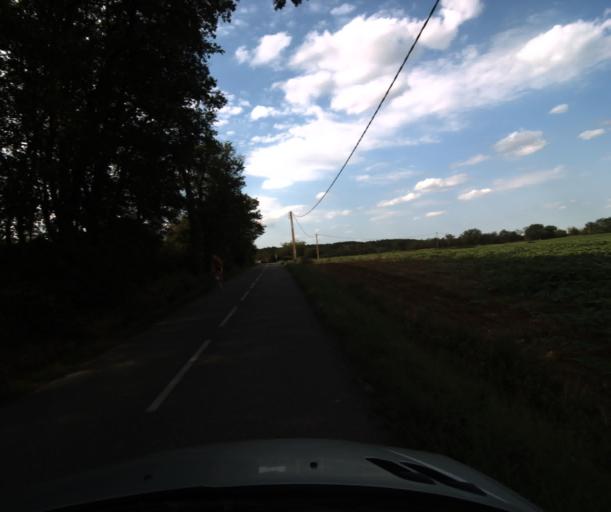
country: FR
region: Midi-Pyrenees
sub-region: Departement de la Haute-Garonne
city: Fonsorbes
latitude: 43.5142
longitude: 1.2215
